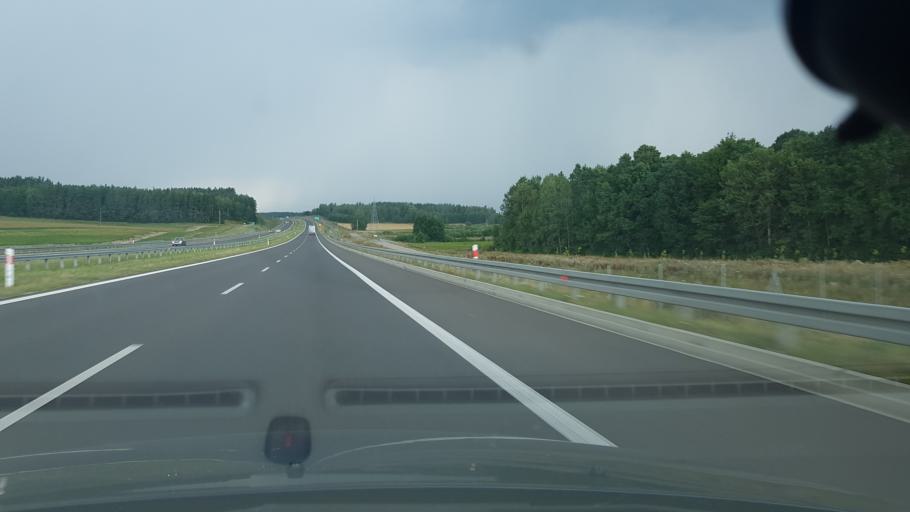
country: PL
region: Warmian-Masurian Voivodeship
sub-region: Powiat nidzicki
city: Nidzica
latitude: 53.3584
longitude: 20.3906
